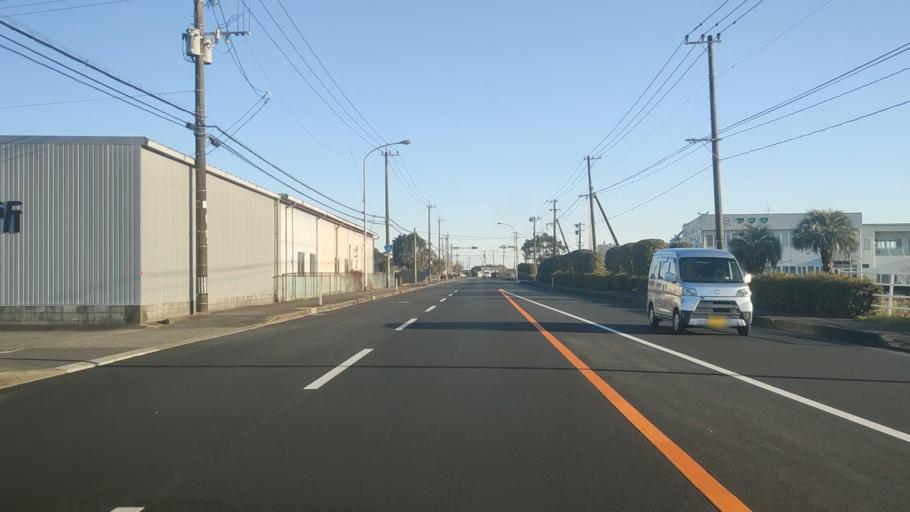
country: JP
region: Miyazaki
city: Takanabe
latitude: 32.2291
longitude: 131.5469
